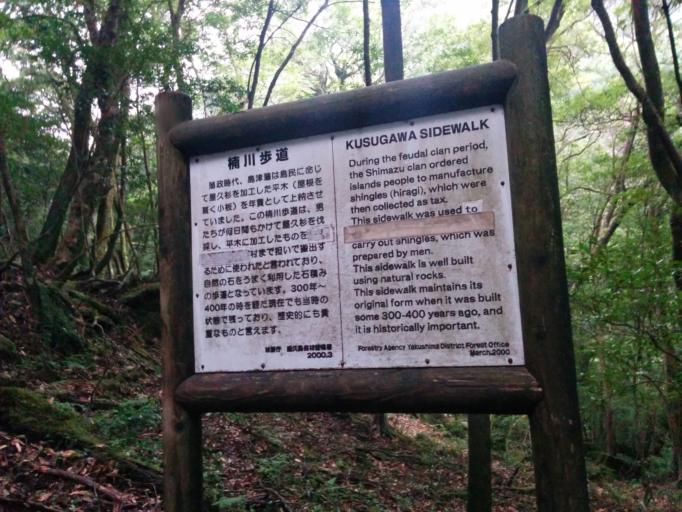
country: JP
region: Kagoshima
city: Nishinoomote
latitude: 30.3766
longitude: 130.5719
